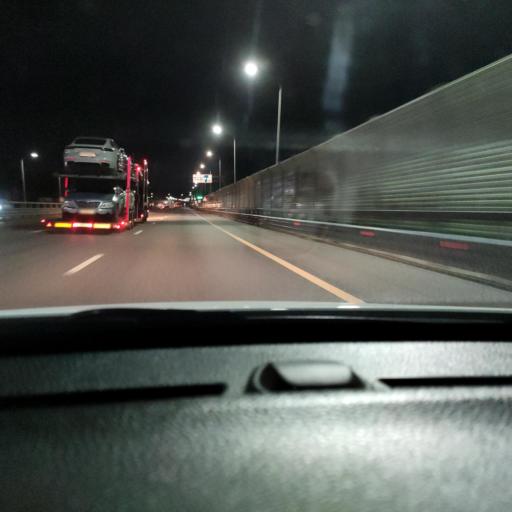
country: RU
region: Voronezj
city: Somovo
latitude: 51.6843
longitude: 39.3023
